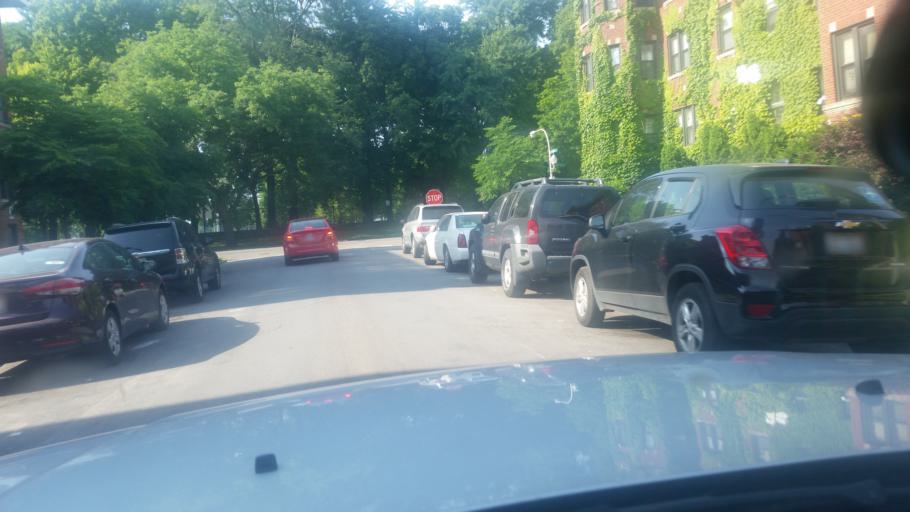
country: US
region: Illinois
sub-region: Cook County
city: Chicago
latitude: 41.7731
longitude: -87.5728
